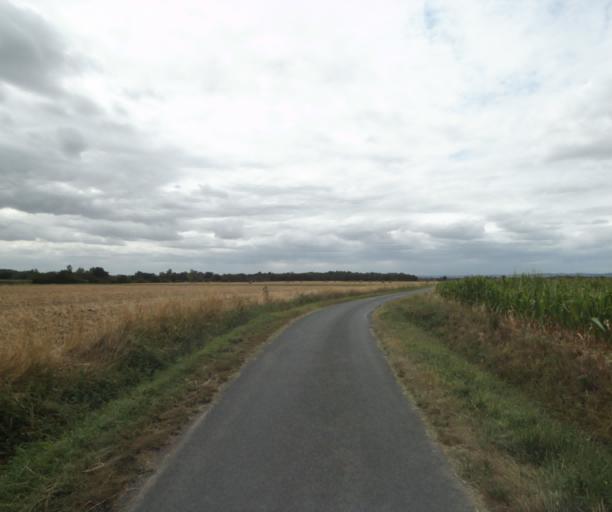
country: FR
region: Midi-Pyrenees
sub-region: Departement du Tarn
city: Soreze
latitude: 43.4636
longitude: 2.0507
